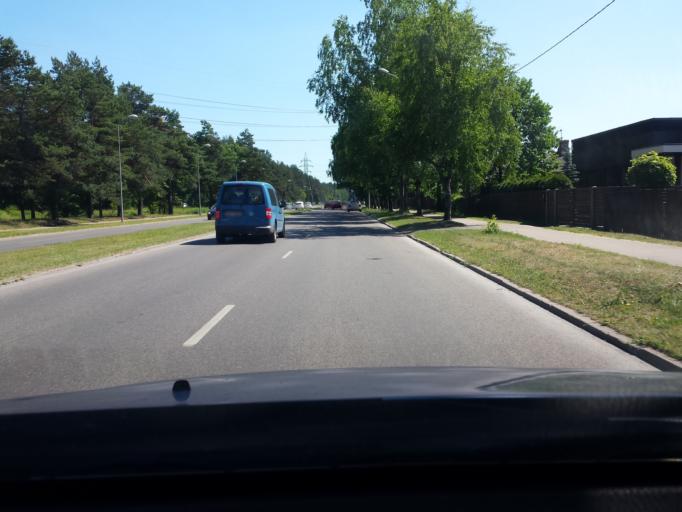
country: LV
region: Riga
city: Jaunciems
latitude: 56.9701
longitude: 24.1940
